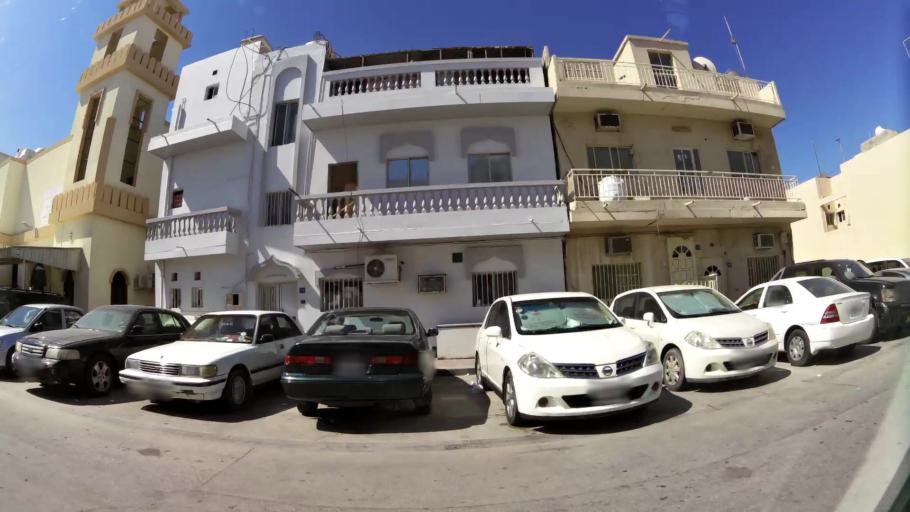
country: BH
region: Muharraq
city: Al Muharraq
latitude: 26.2477
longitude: 50.6175
